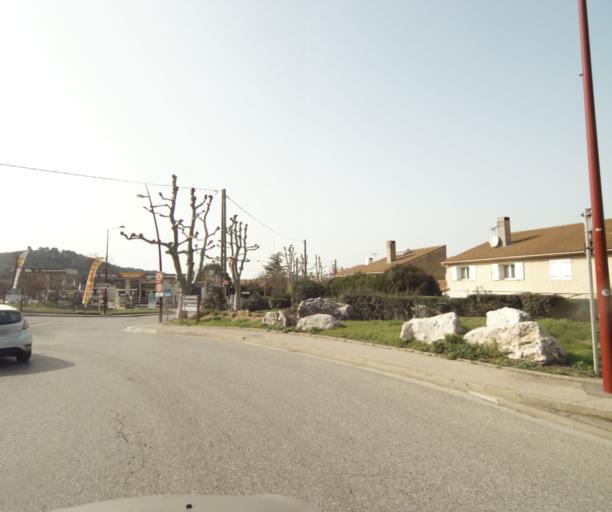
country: FR
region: Provence-Alpes-Cote d'Azur
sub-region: Departement des Bouches-du-Rhone
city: Les Pennes-Mirabeau
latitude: 43.4094
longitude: 5.3217
